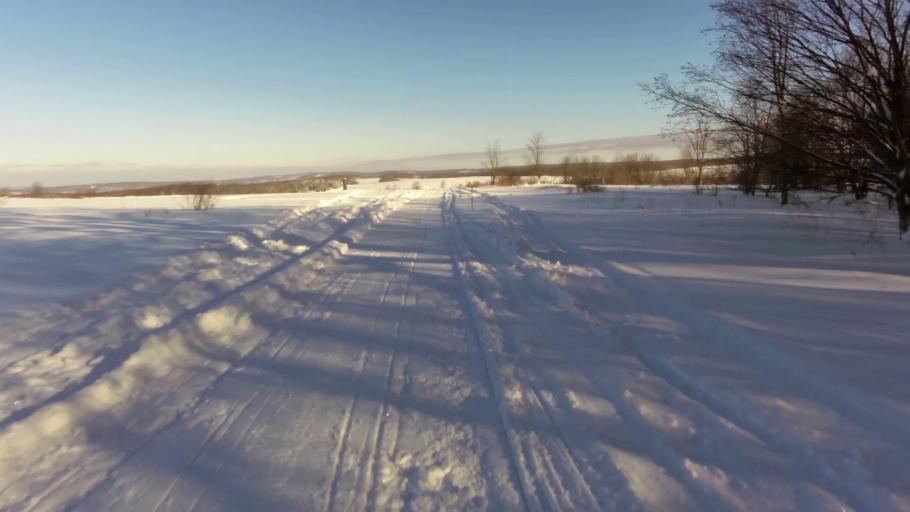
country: US
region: New York
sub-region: Chautauqua County
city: Falconer
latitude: 42.2528
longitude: -79.2132
